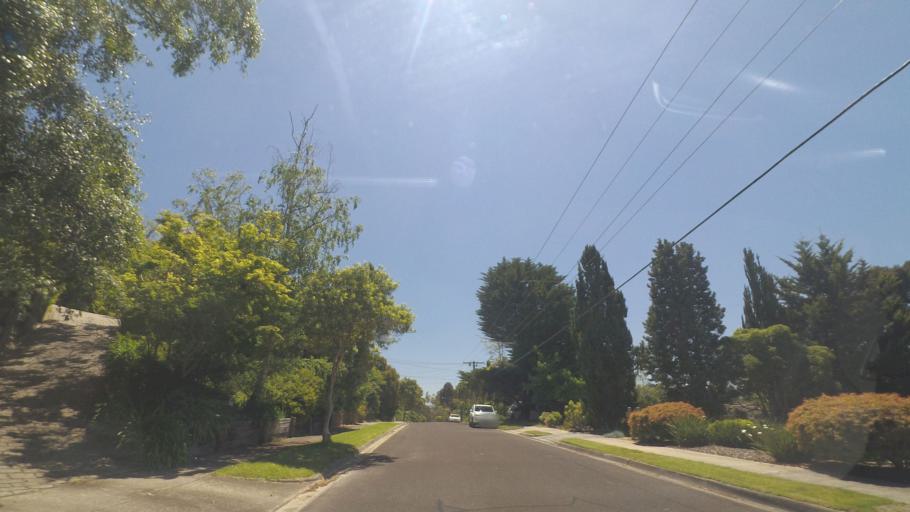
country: AU
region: Victoria
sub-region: Maroondah
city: Croydon North
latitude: -37.7663
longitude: 145.2857
